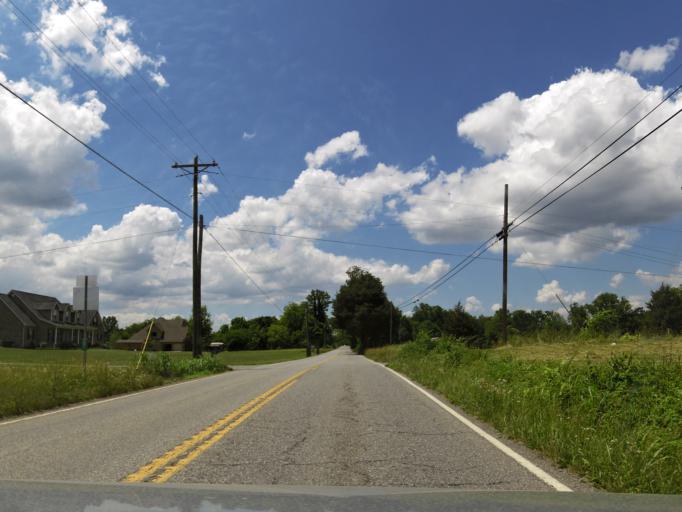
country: US
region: Tennessee
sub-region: Loudon County
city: Greenback
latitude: 35.6661
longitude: -84.0528
